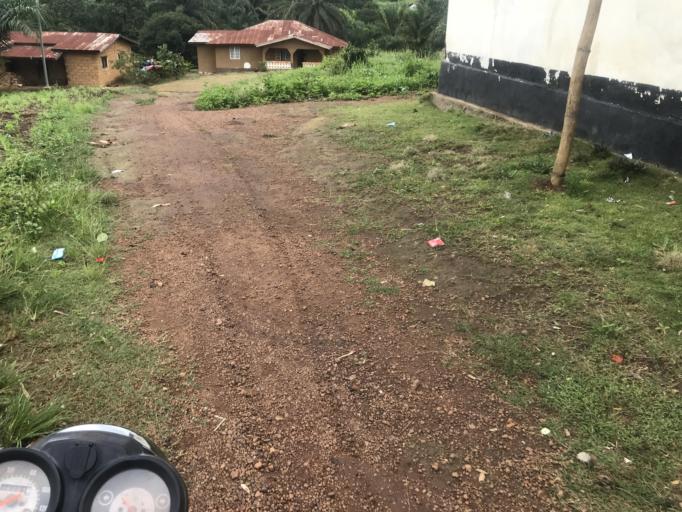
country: SL
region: Eastern Province
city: Buedu
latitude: 8.4619
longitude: -10.3331
